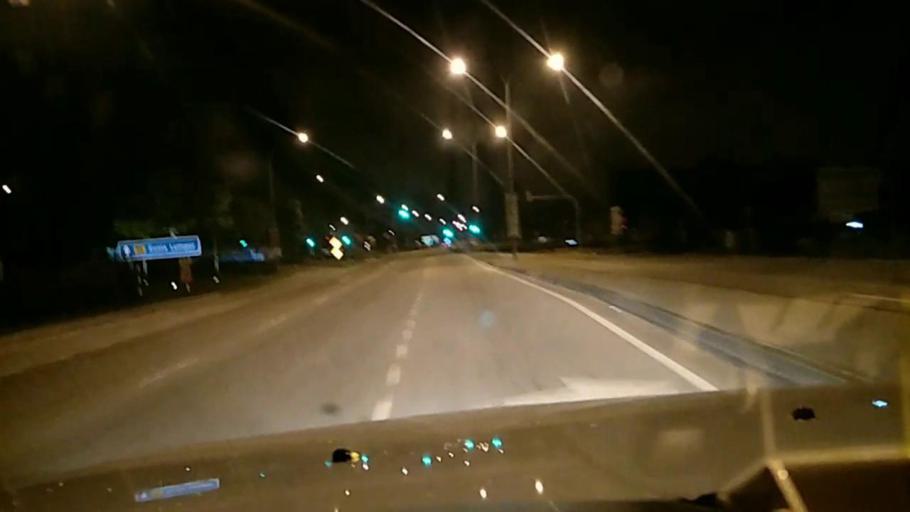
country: MY
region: Selangor
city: Ladang Seri Kundang
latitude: 3.2478
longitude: 101.4719
